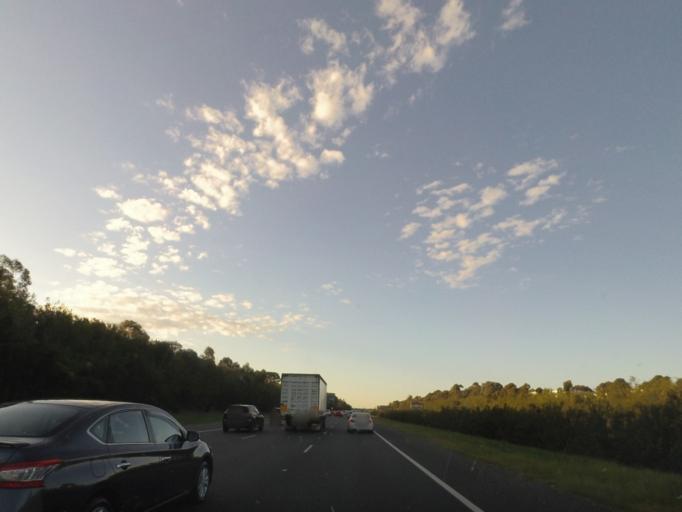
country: AU
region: Victoria
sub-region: Knox
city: Wantirna South
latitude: -37.8972
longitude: 145.2148
